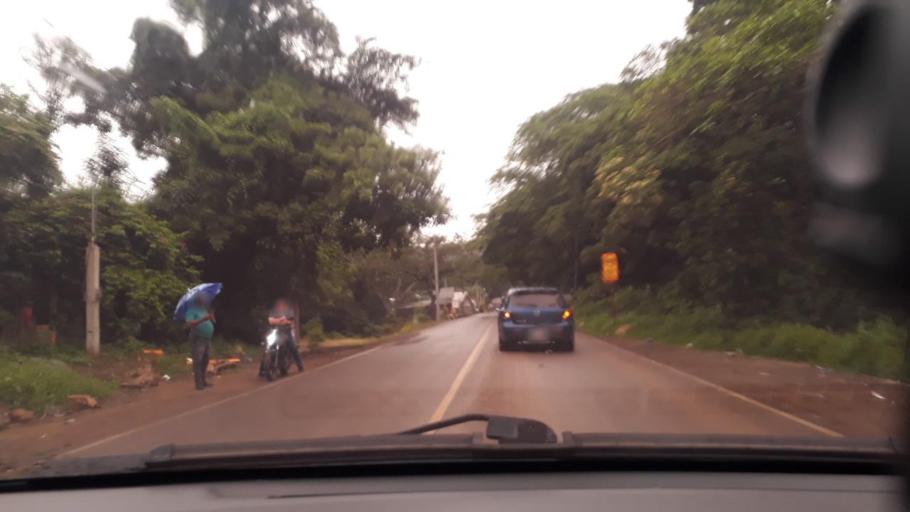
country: GT
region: Jutiapa
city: Atescatempa
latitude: 14.1961
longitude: -89.6753
